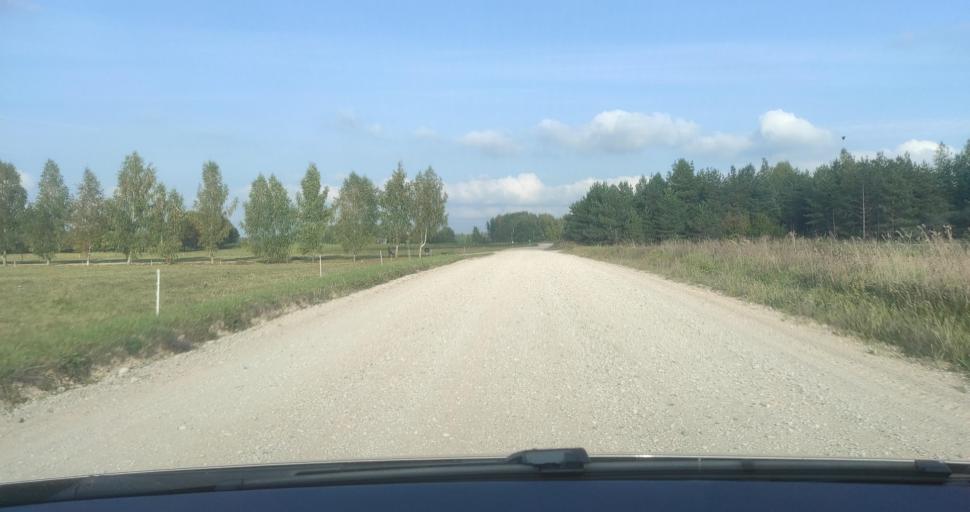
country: LV
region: Alsunga
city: Alsunga
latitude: 57.0002
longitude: 21.5905
